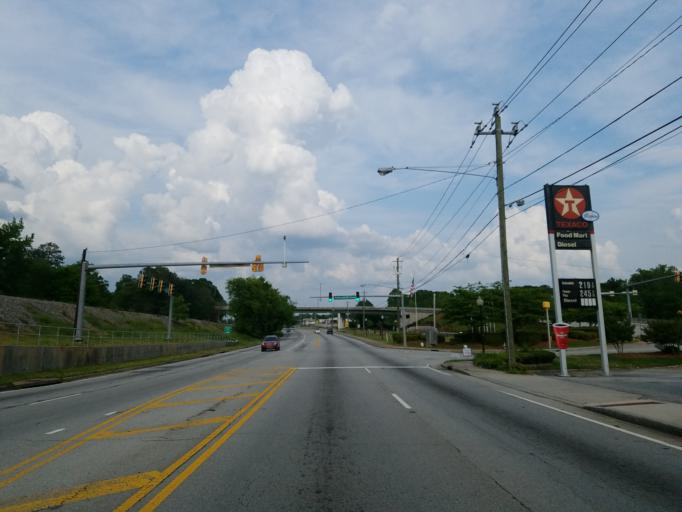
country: US
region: Georgia
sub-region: Cobb County
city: Austell
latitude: 33.8134
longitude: -84.6317
